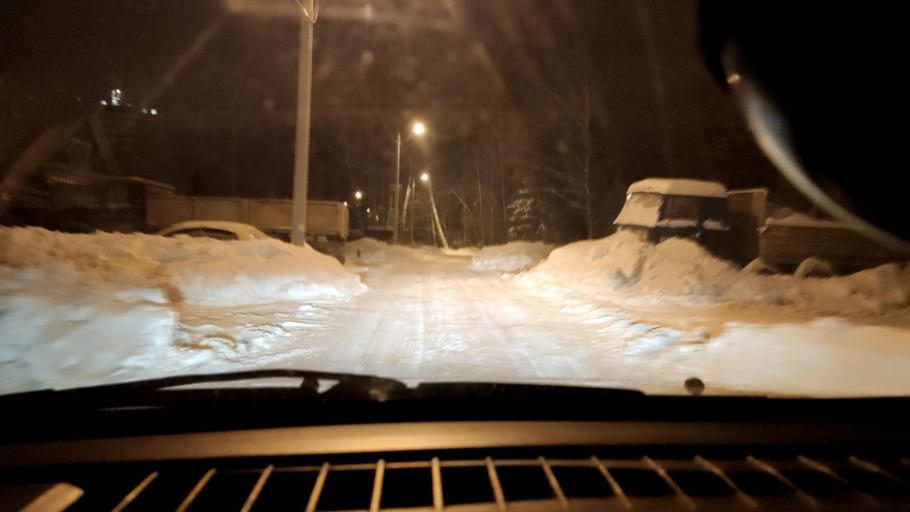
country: RU
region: Perm
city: Kondratovo
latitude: 58.0256
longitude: 55.9940
